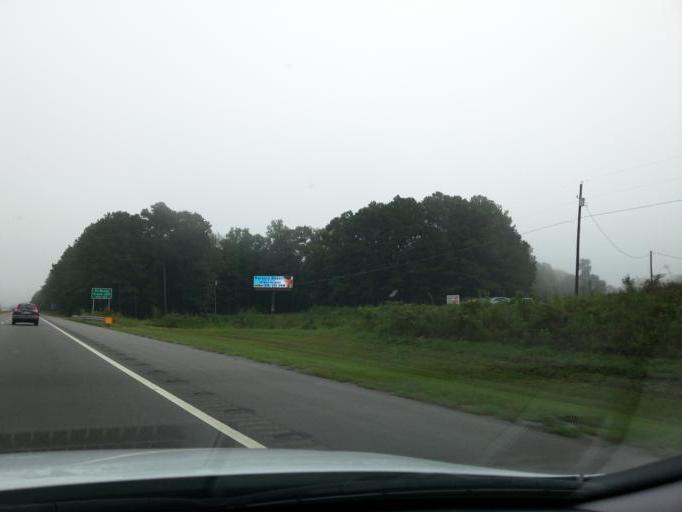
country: US
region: North Carolina
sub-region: Cumberland County
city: Fort Bragg
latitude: 35.0842
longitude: -78.9651
